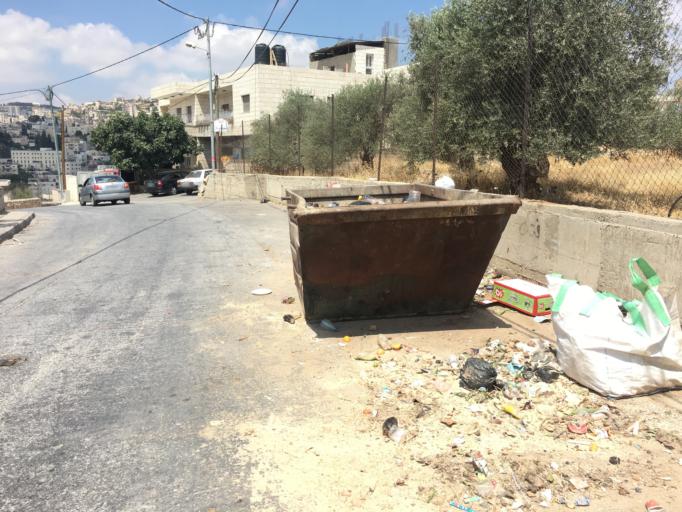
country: PS
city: Khallat Hamamah
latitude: 31.7186
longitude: 35.1963
